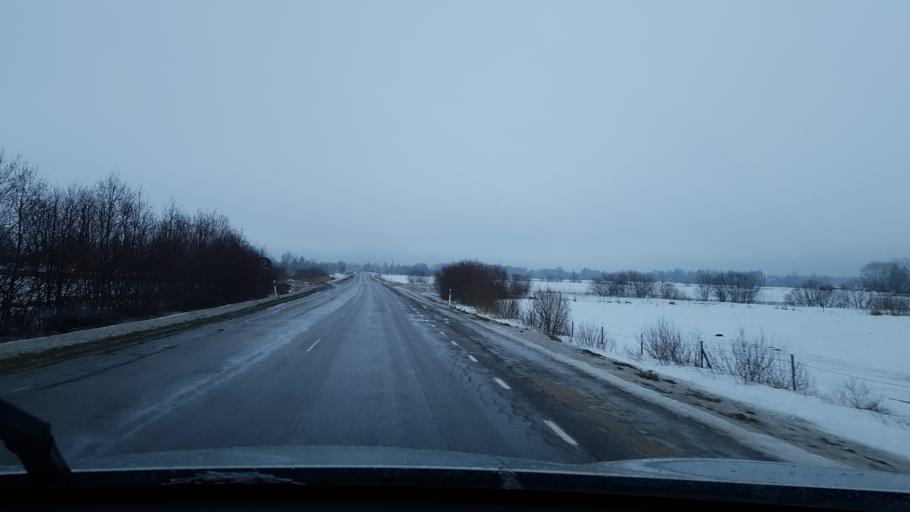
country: EE
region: Harju
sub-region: Nissi vald
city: Turba
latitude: 58.9103
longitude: 24.1445
